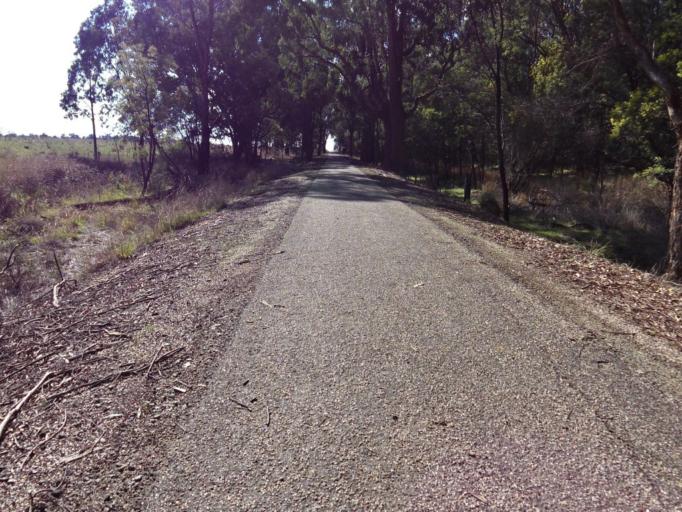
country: AU
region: Victoria
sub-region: Wangaratta
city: Wangaratta
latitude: -36.4000
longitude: 146.6466
